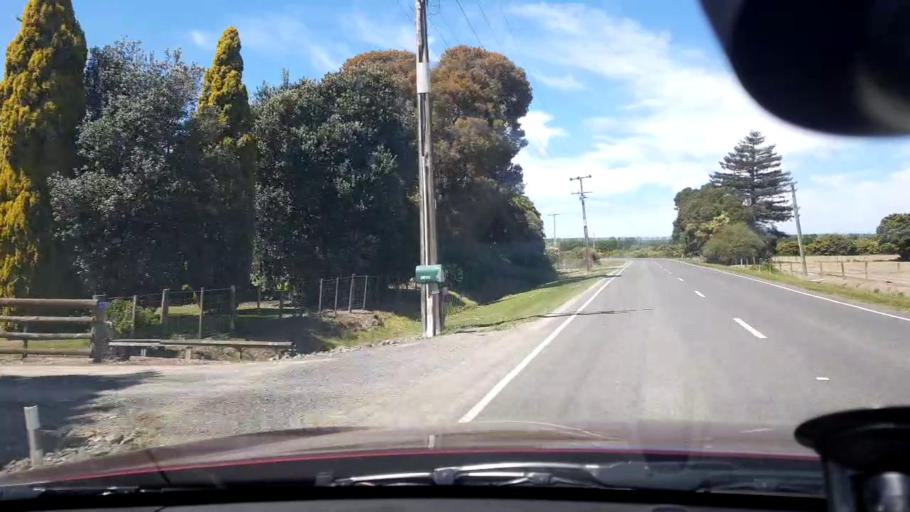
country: NZ
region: Gisborne
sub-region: Gisborne District
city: Gisborne
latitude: -38.6367
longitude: 177.9307
